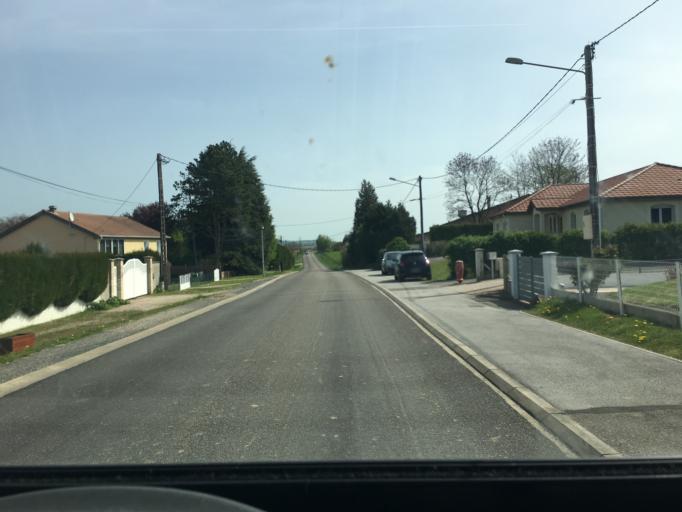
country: FR
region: Lorraine
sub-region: Departement de Meurthe-et-Moselle
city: Fleville-devant-Nancy
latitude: 48.6115
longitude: 6.2415
